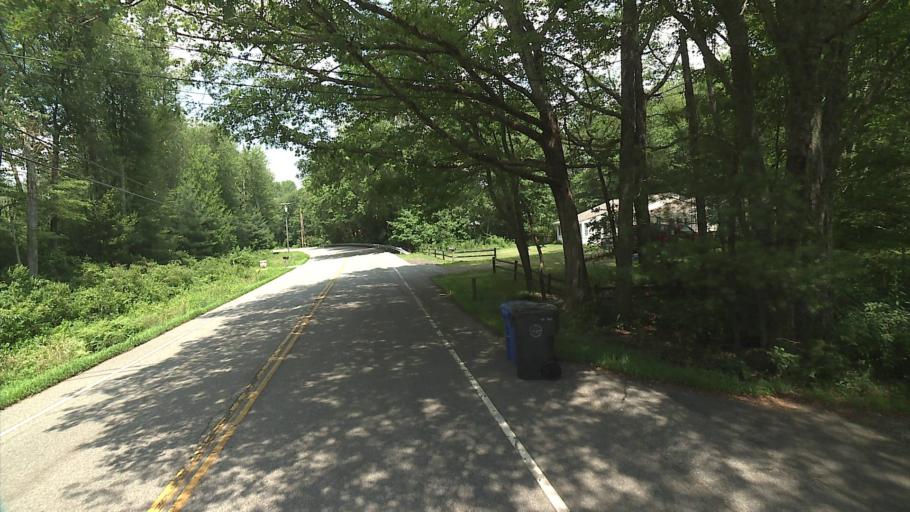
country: US
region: Rhode Island
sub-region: Washington County
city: Hopkinton
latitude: 41.5610
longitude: -71.8144
